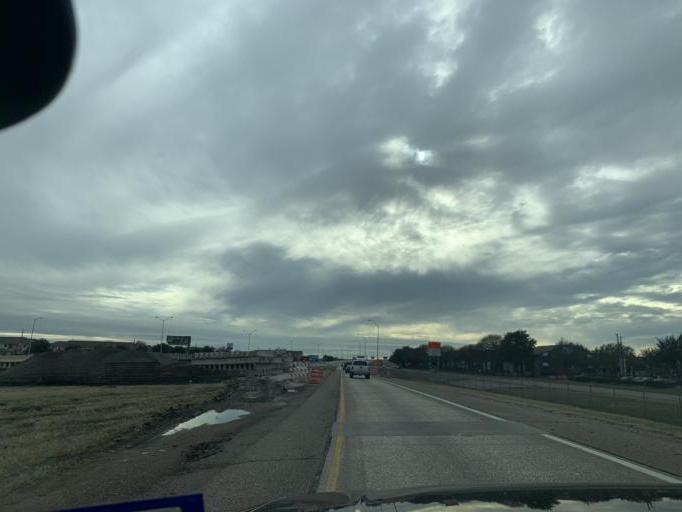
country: US
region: Texas
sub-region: Dallas County
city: Duncanville
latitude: 32.6529
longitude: -96.8803
